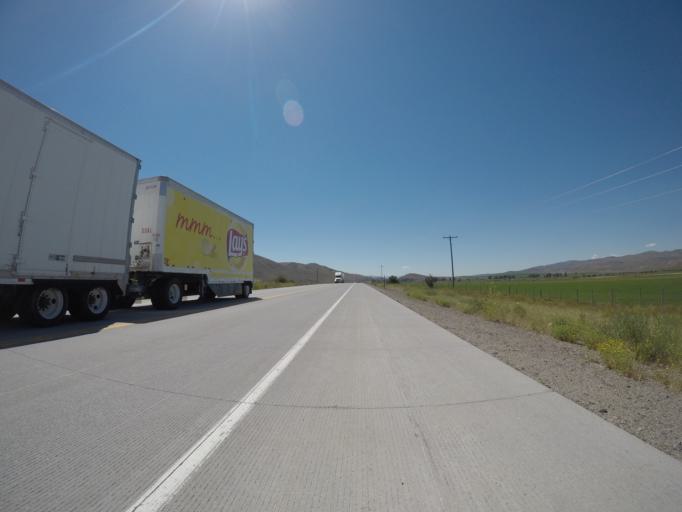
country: US
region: Idaho
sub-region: Bear Lake County
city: Montpelier
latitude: 42.1580
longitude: -110.9844
